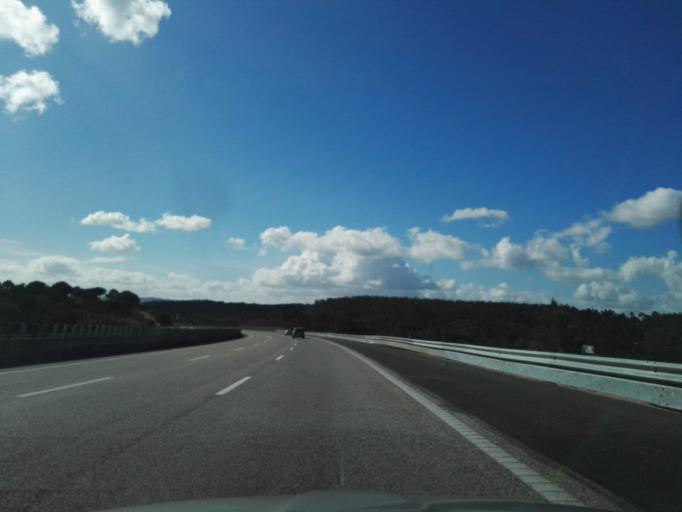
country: PT
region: Lisbon
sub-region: Azambuja
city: Aveiras de Cima
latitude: 39.1127
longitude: -8.9285
